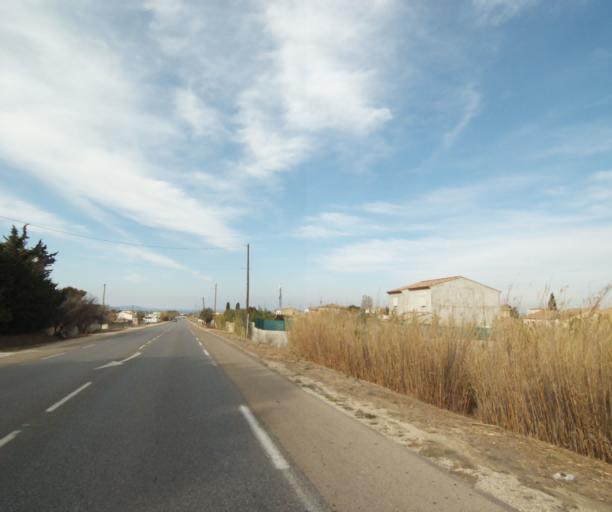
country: FR
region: Provence-Alpes-Cote d'Azur
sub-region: Departement des Bouches-du-Rhone
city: Gignac-la-Nerthe
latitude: 43.3862
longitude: 5.2168
